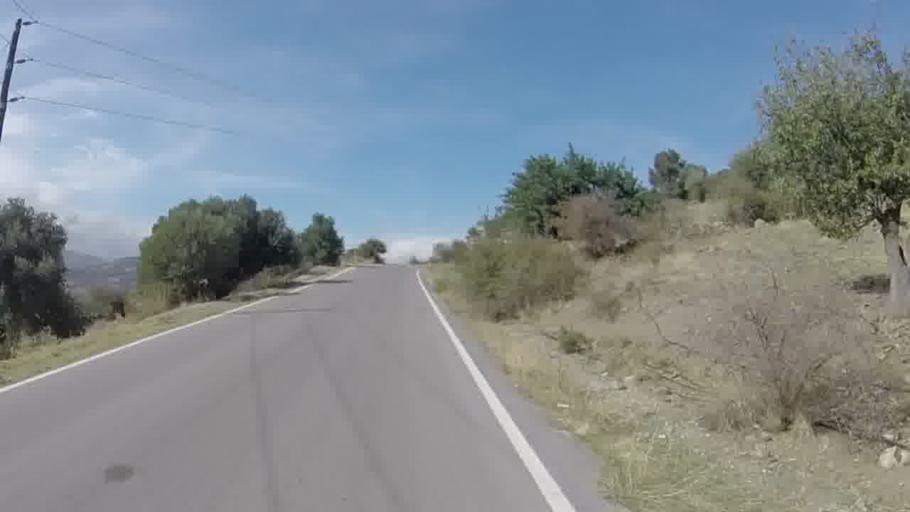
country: GR
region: Crete
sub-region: Nomos Rethymnis
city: Agia Galini
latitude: 35.1475
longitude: 24.7367
